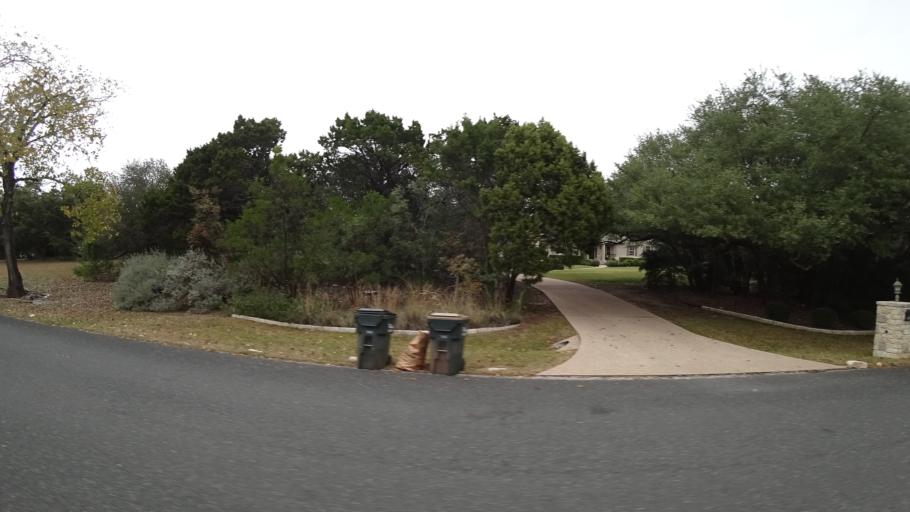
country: US
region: Texas
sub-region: Travis County
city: West Lake Hills
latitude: 30.3754
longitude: -97.8180
